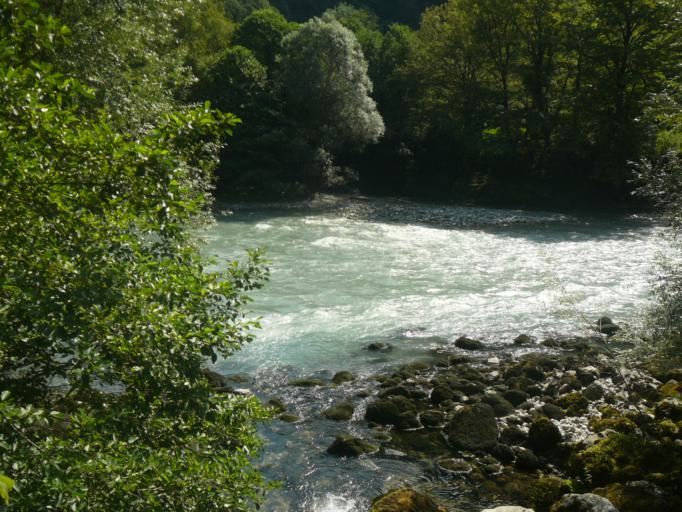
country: GE
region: Abkhazia
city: Gagra
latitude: 43.3508
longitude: 40.4124
